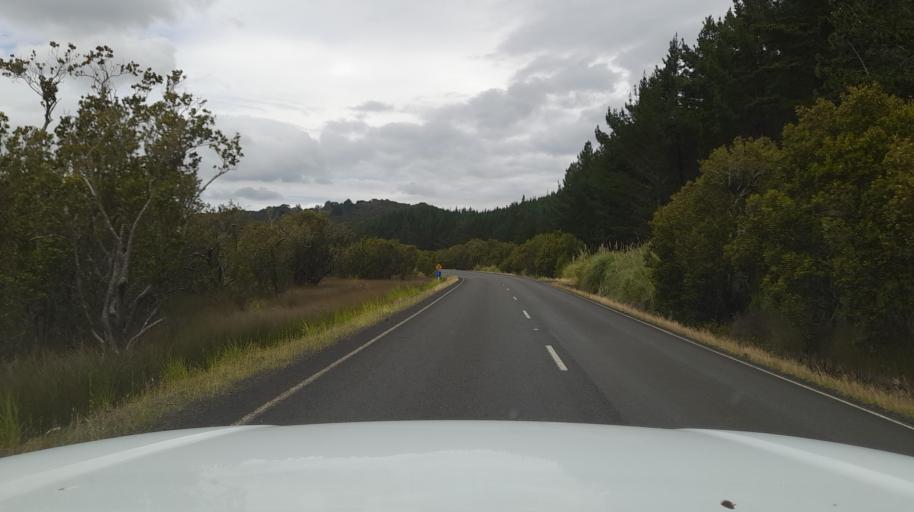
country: NZ
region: Northland
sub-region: Far North District
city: Kaitaia
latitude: -35.3637
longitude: 173.4392
